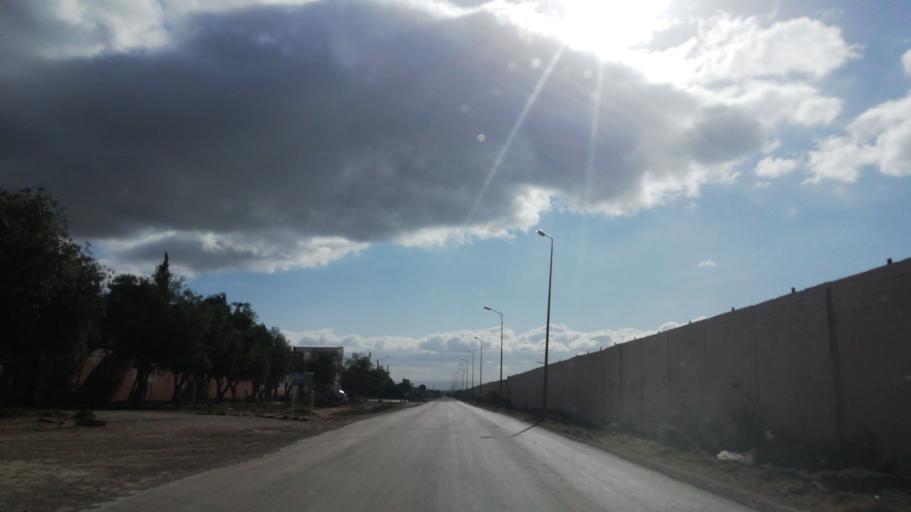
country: DZ
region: Oran
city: Es Senia
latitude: 35.6403
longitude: -0.6005
